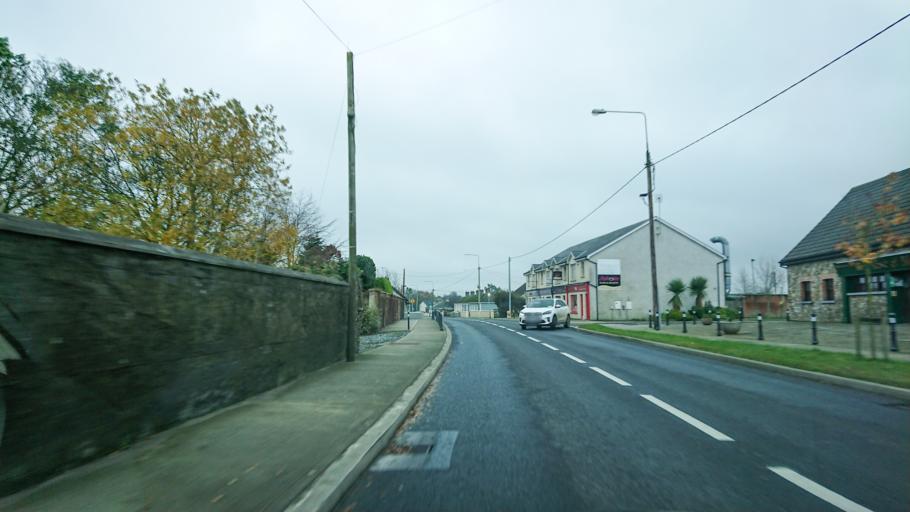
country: IE
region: Leinster
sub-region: Kilkenny
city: Mooncoin
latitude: 52.2926
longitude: -7.2549
